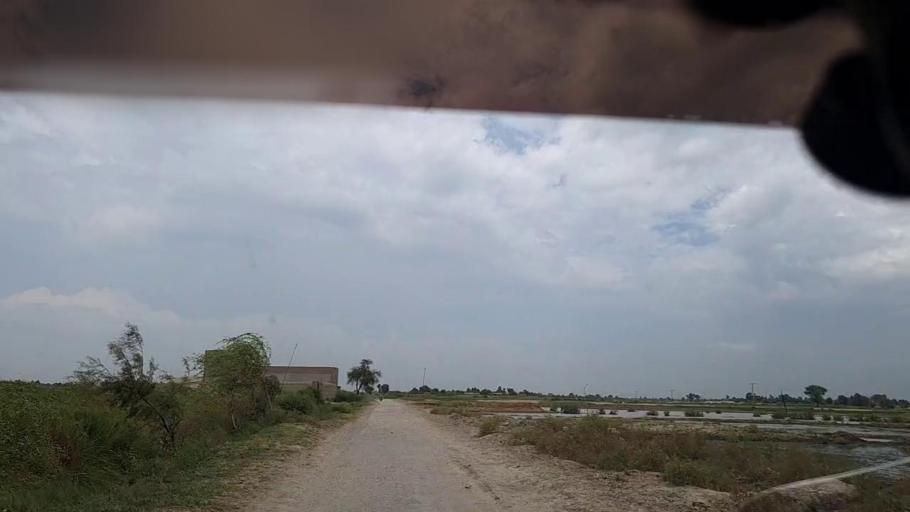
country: PK
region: Sindh
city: Ghauspur
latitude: 28.1120
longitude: 68.9857
